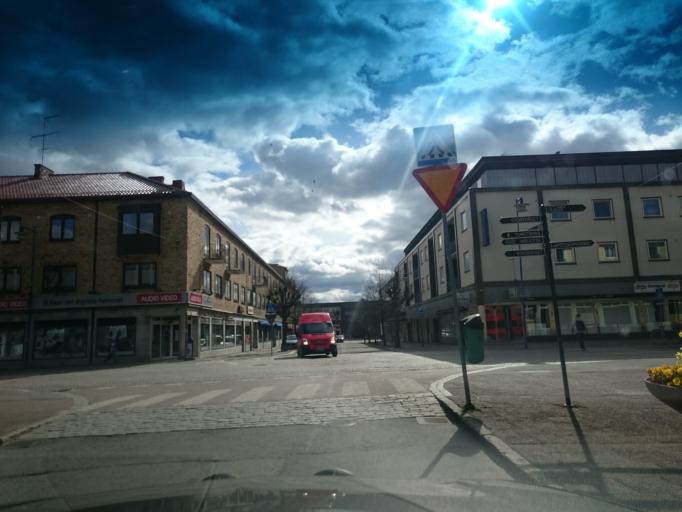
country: SE
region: Joenkoeping
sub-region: Vetlanda Kommun
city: Vetlanda
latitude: 57.4270
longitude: 15.0835
